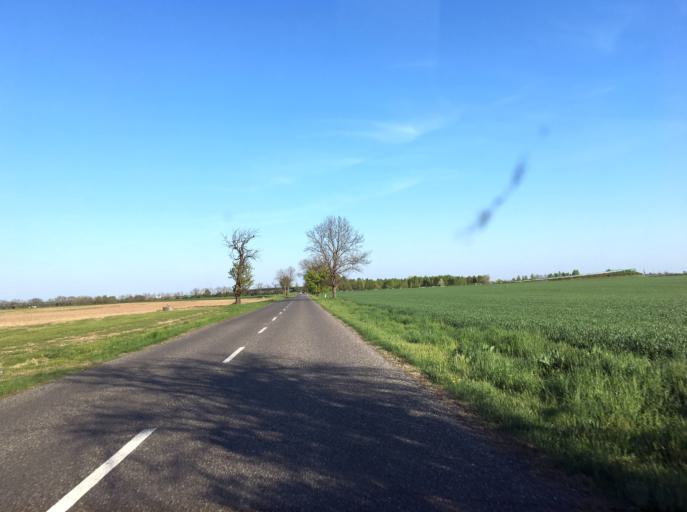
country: AT
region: Burgenland
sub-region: Politischer Bezirk Neusiedl am See
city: Kittsee
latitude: 48.0755
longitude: 17.0860
